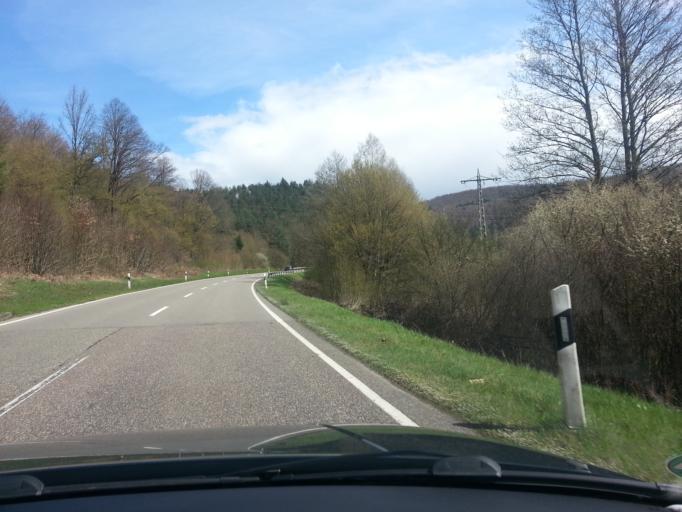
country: DE
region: Rheinland-Pfalz
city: Munchweiler an der Rodalbe
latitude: 49.2357
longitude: 7.6885
